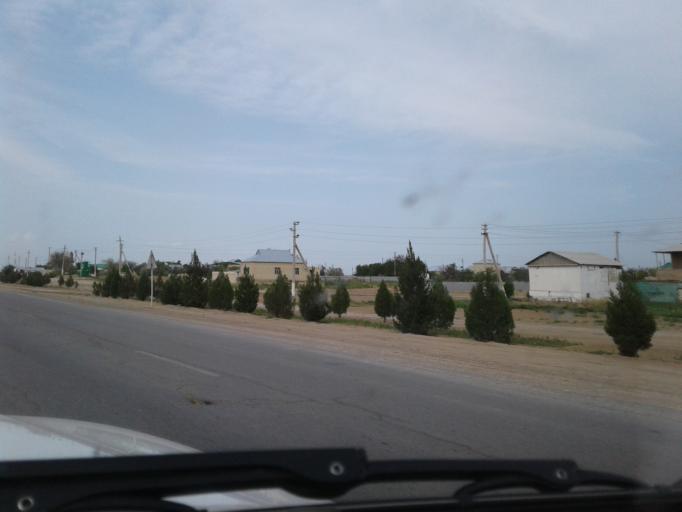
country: TM
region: Mary
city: Mary
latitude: 37.5192
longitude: 61.7231
